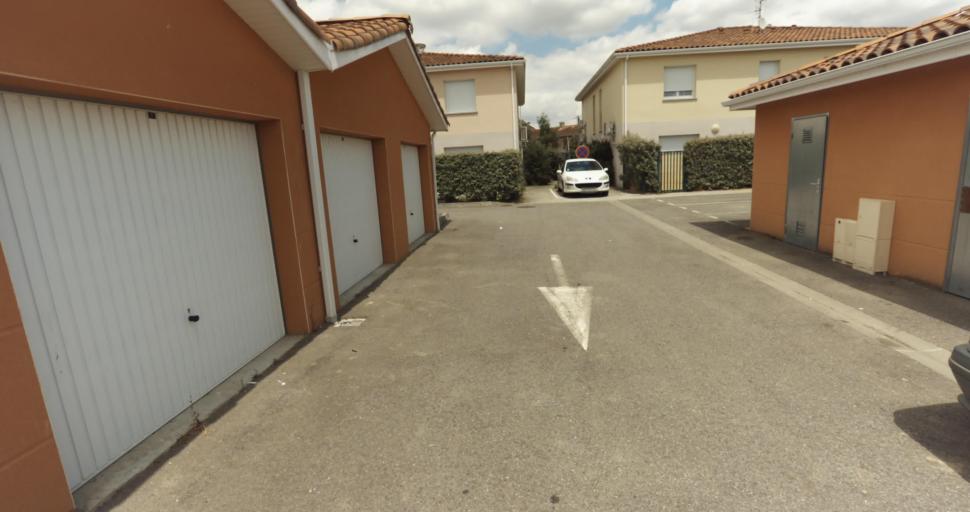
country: FR
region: Midi-Pyrenees
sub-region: Departement de la Haute-Garonne
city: Fontenilles
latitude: 43.5524
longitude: 1.1836
